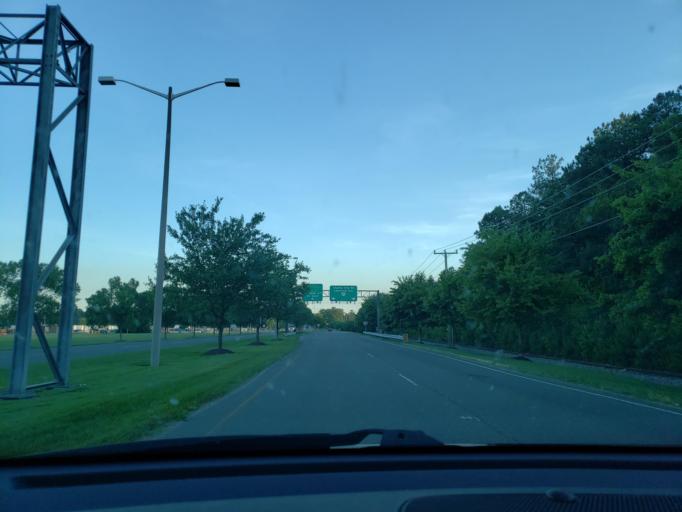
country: US
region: Virginia
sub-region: Henrico County
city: Fort Lee
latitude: 37.5036
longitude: -77.3385
